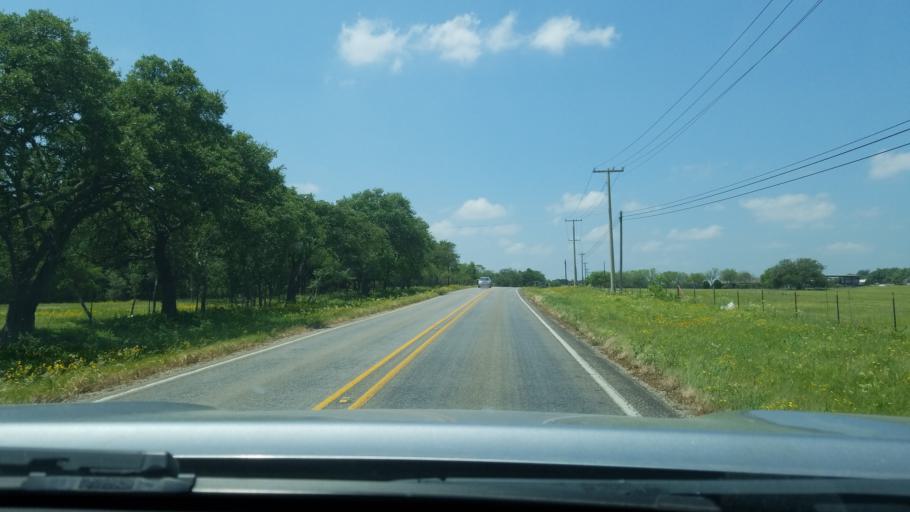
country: US
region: Texas
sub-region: Hays County
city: Woodcreek
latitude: 30.0237
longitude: -98.1606
